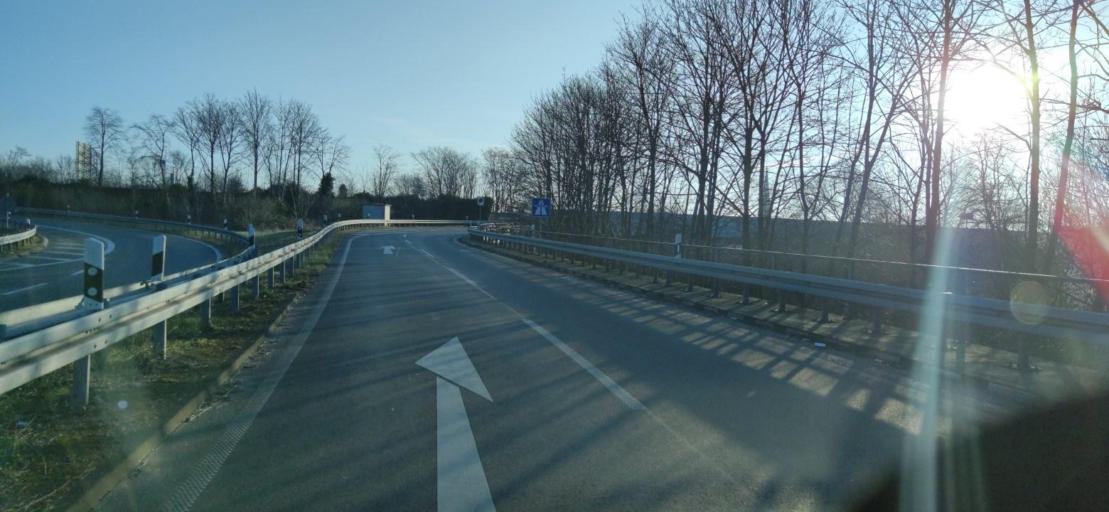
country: DE
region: North Rhine-Westphalia
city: Meiderich
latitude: 51.4682
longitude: 6.7646
